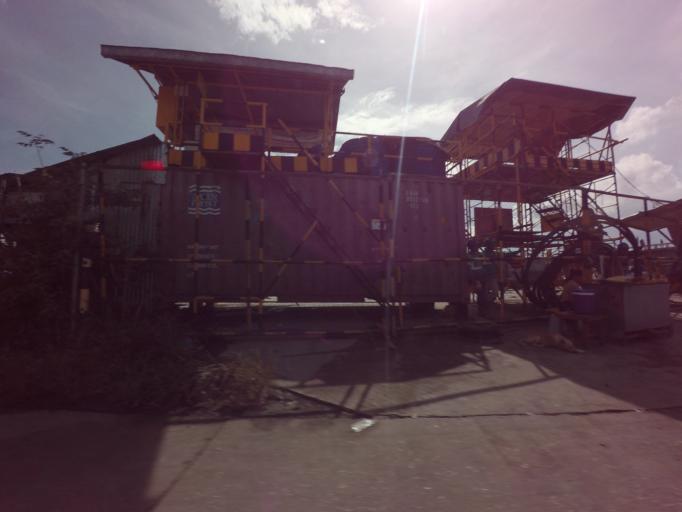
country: PH
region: Calabarzon
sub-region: Province of Rizal
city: Taguig
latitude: 14.5351
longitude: 121.1014
